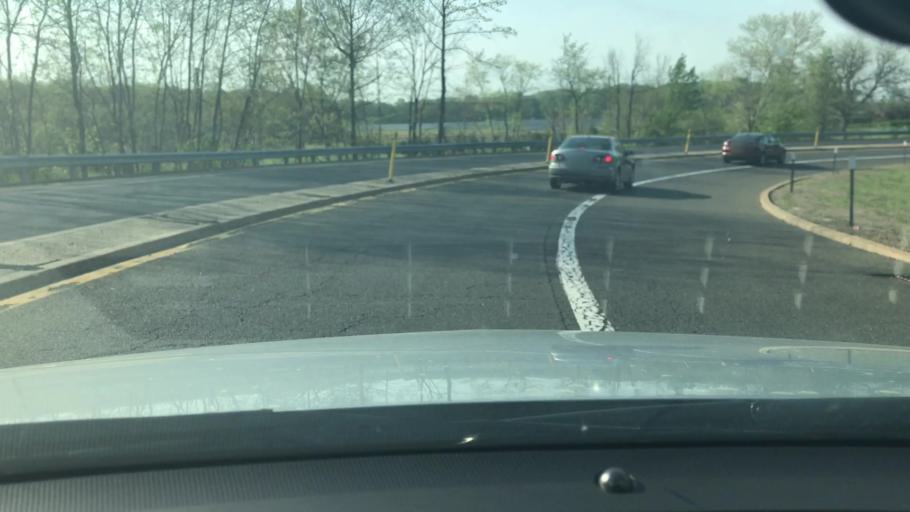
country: US
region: New Jersey
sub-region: Burlington County
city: Willingboro
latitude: 40.0263
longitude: -74.8235
